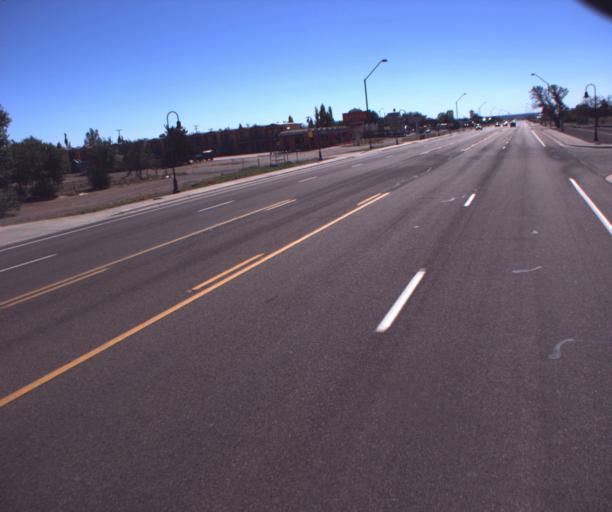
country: US
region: Arizona
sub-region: Navajo County
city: Holbrook
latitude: 34.9314
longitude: -110.1383
